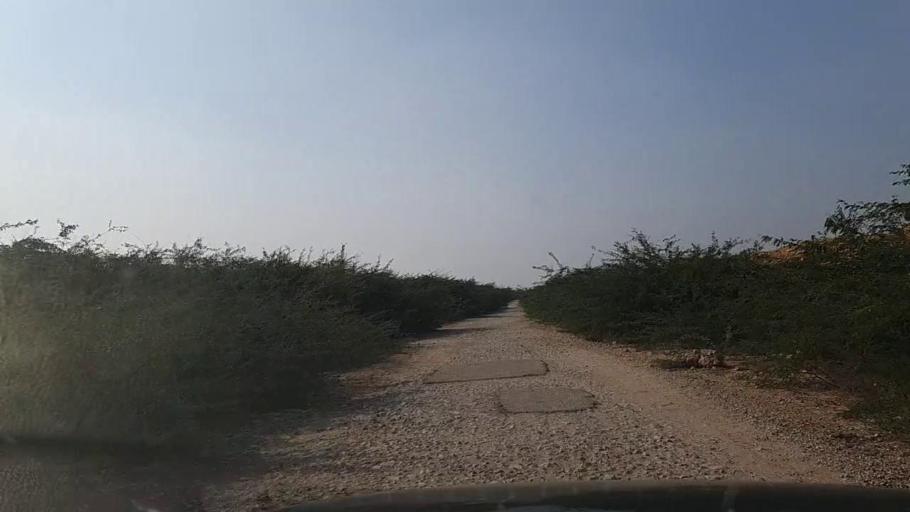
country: PK
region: Sindh
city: Gharo
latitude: 24.7537
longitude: 67.5362
